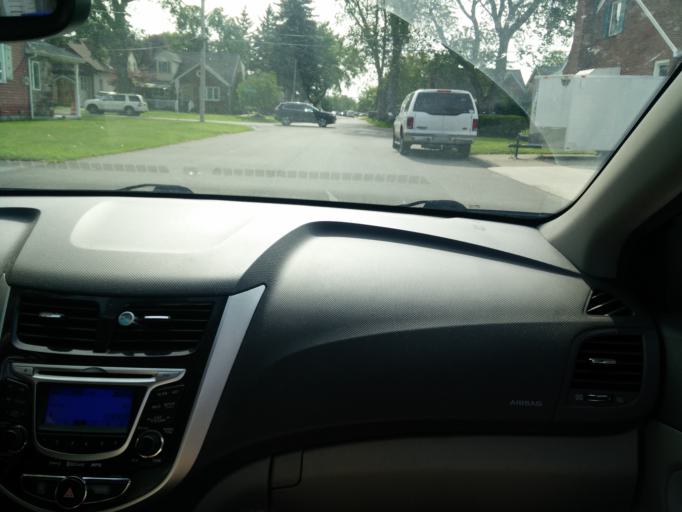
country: US
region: New York
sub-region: Erie County
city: West Seneca
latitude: 42.8364
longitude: -78.7993
